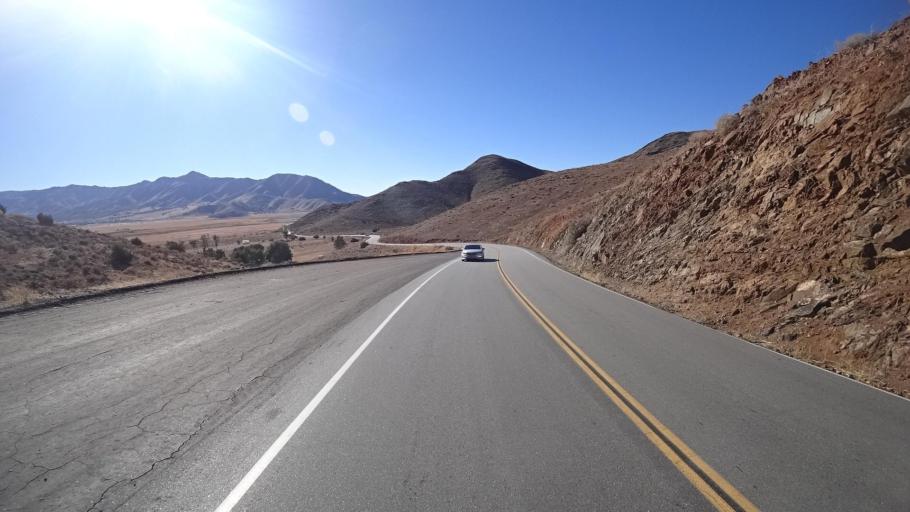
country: US
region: California
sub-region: Kern County
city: Wofford Heights
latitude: 35.6821
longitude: -118.3912
